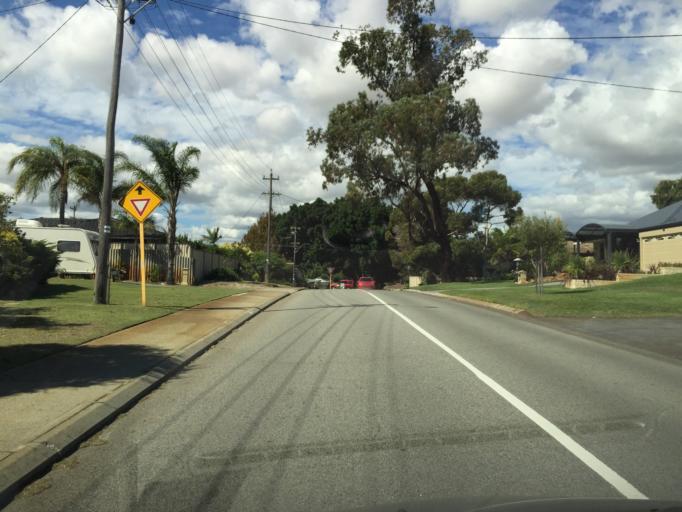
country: AU
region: Western Australia
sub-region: Canning
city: Willetton
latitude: -32.0583
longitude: 115.8912
